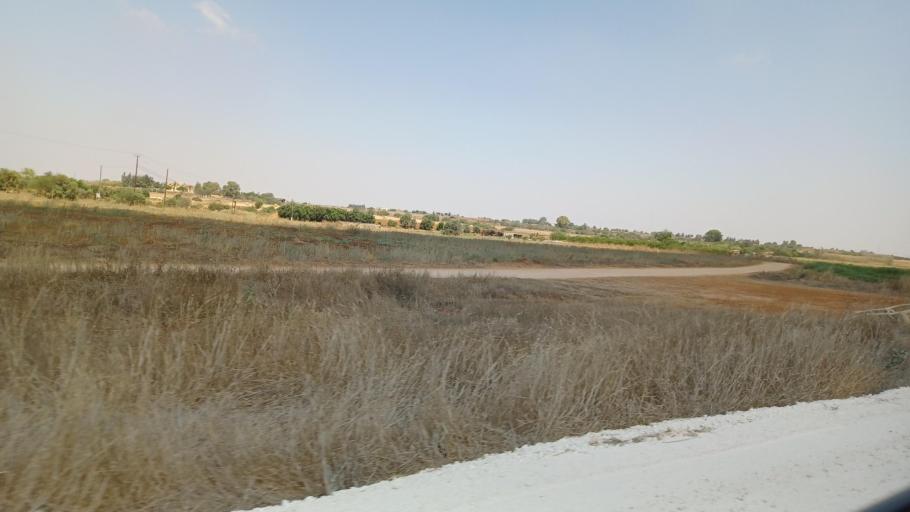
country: CY
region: Ammochostos
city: Frenaros
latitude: 35.0599
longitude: 33.9210
